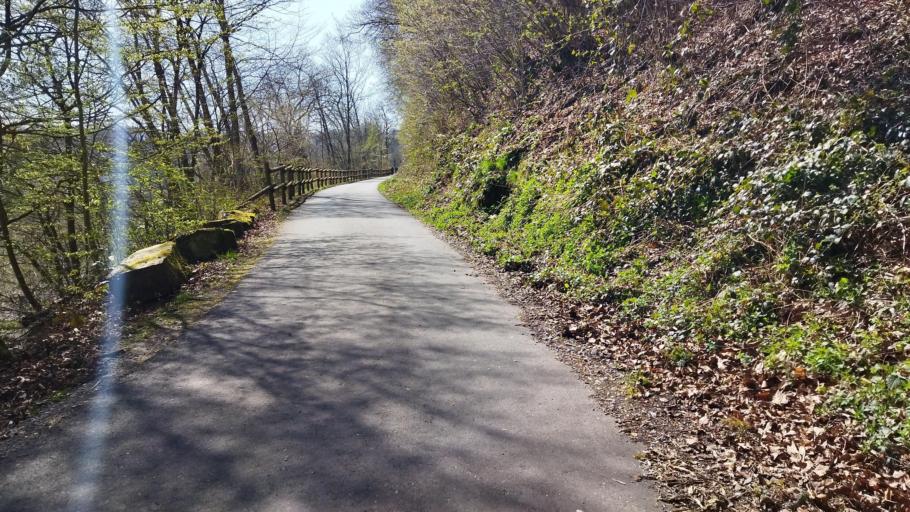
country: DE
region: Lower Saxony
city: Bad Karlshafen
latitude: 51.6495
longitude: 9.4559
